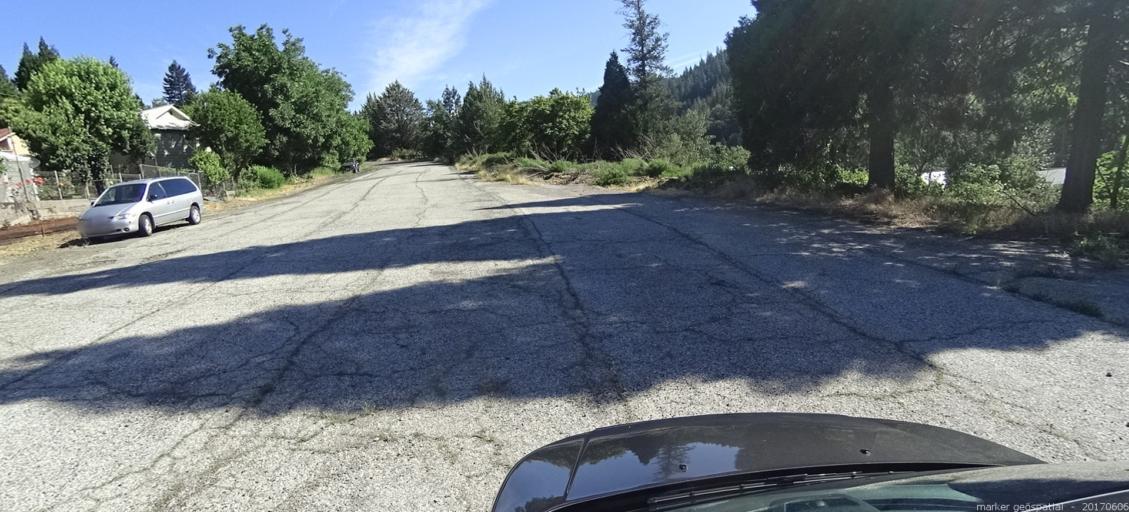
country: US
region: California
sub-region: Siskiyou County
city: Dunsmuir
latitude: 41.2006
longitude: -122.2742
